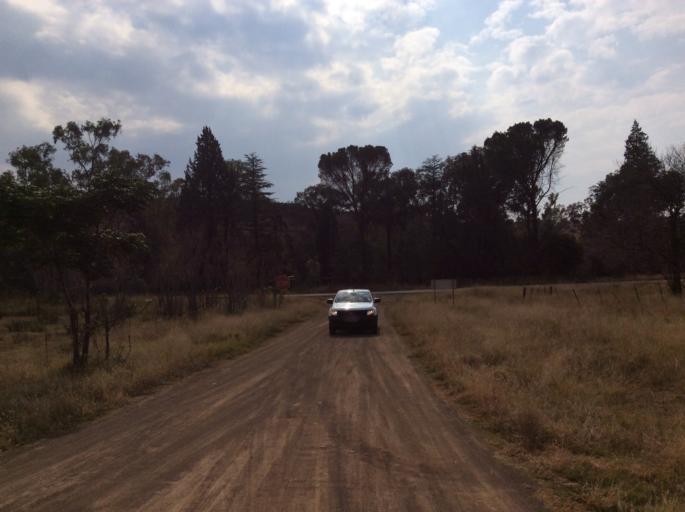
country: LS
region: Mafeteng
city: Mafeteng
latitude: -29.7354
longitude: 27.0471
